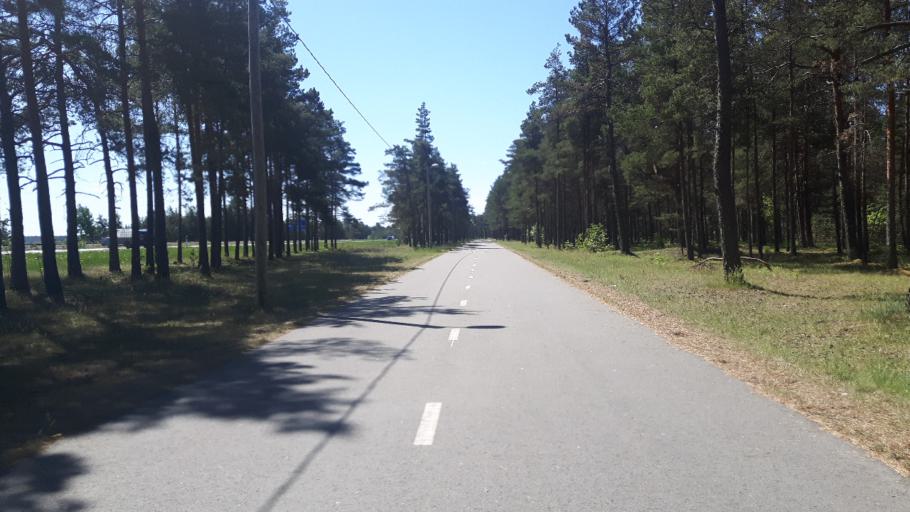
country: EE
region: Harju
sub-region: Saku vald
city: Saku
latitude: 59.3600
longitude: 24.7149
